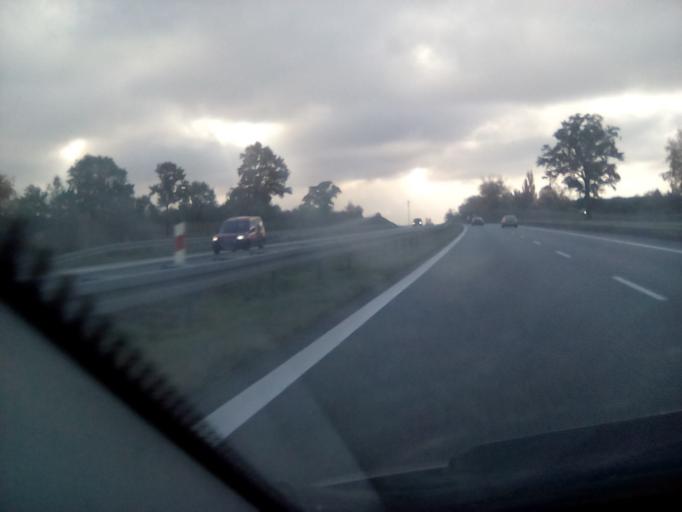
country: PL
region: Masovian Voivodeship
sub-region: Powiat bialobrzeski
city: Promna
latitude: 51.6854
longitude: 20.9361
